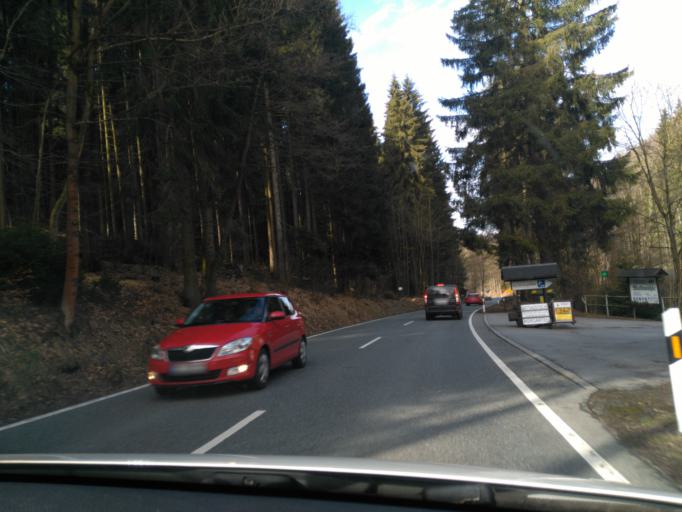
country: DE
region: Saxony
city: Wolkenstein
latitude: 50.6657
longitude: 13.0701
